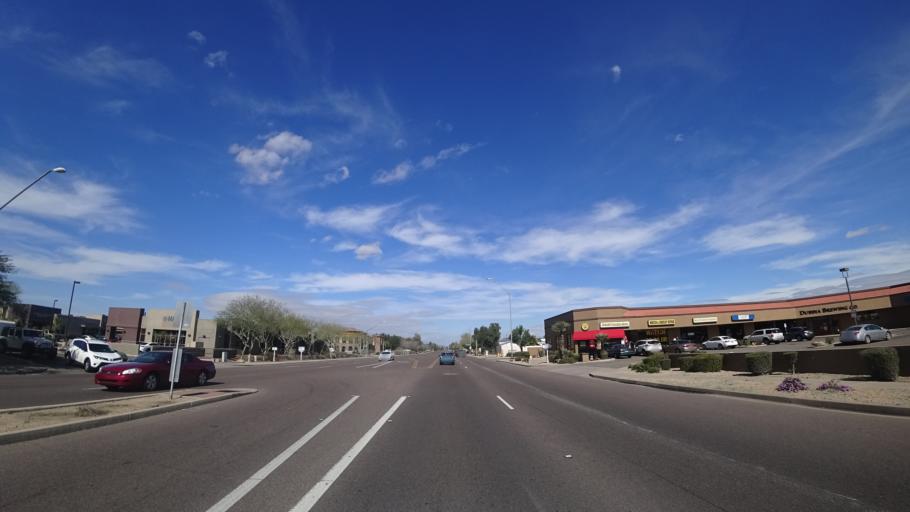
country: US
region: Arizona
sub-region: Maricopa County
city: Peoria
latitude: 33.6393
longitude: -112.2029
